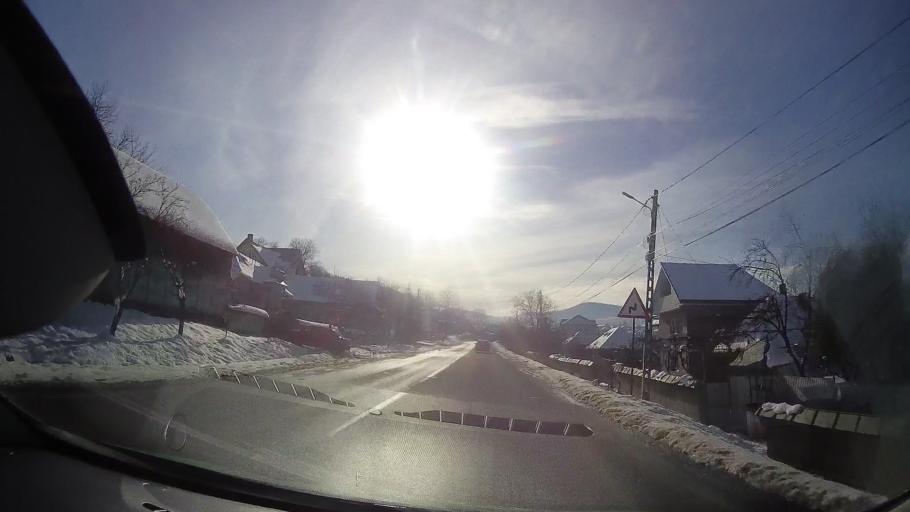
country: RO
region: Neamt
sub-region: Comuna Baltatesti
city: Valea Seaca
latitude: 47.1285
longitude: 26.3142
